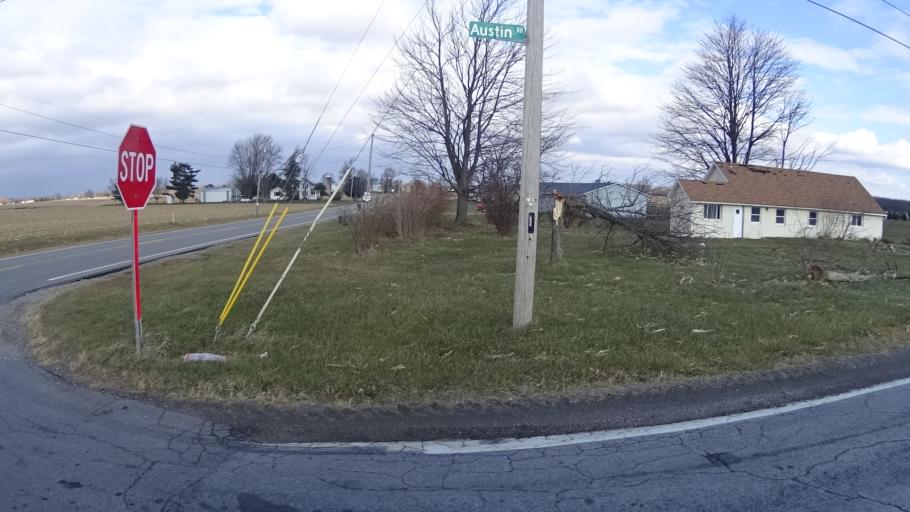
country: US
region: Ohio
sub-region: Lorain County
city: Camden
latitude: 41.2050
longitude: -82.3066
